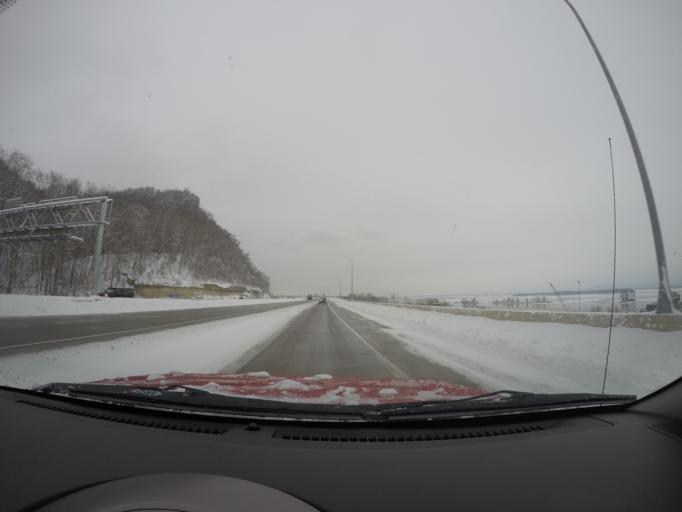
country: US
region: Minnesota
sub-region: Houston County
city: La Crescent
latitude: 43.8641
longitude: -91.3111
